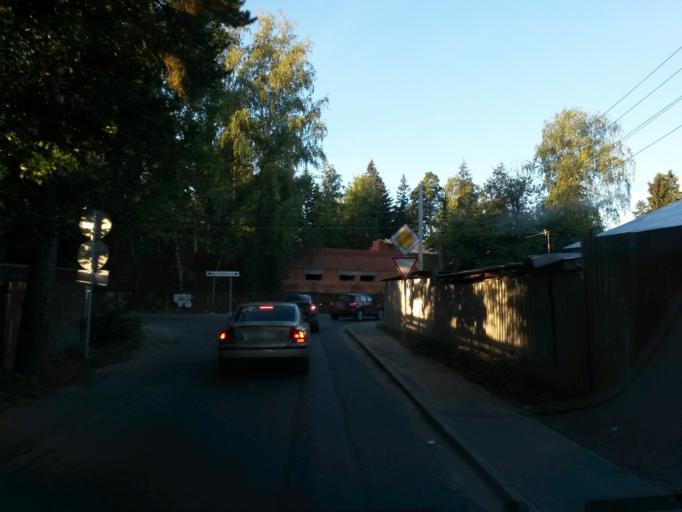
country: RU
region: Moskovskaya
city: Mamontovka
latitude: 55.9799
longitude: 37.8425
